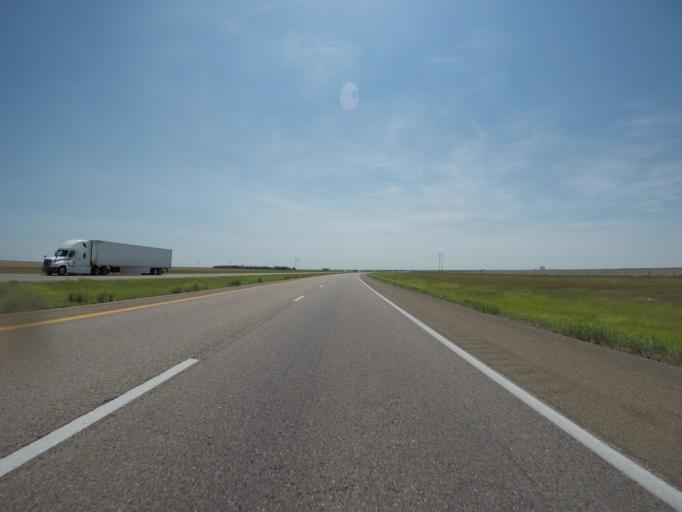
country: US
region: Kansas
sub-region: Thomas County
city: Colby
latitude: 39.3093
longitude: -100.9687
